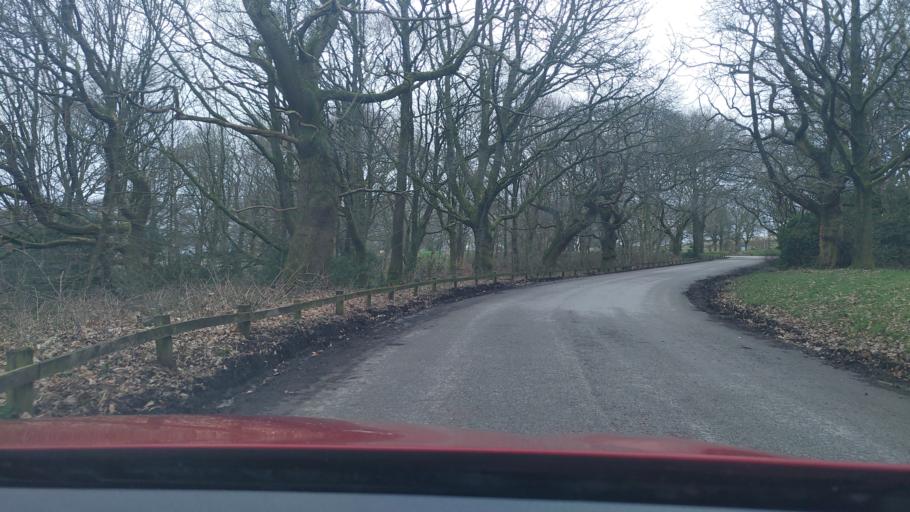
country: GB
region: England
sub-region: Borough of Bolton
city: Horwich
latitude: 53.6252
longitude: -2.5583
